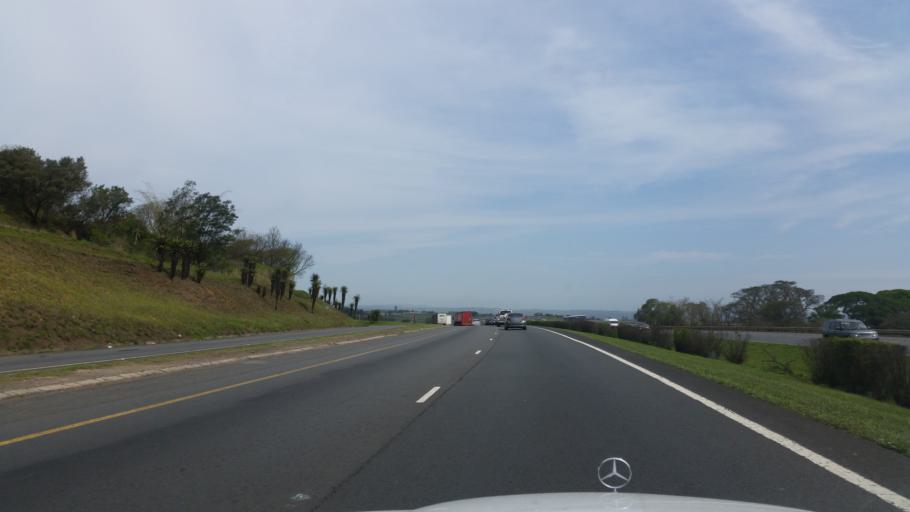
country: ZA
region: KwaZulu-Natal
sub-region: uMgungundlovu District Municipality
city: Camperdown
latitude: -29.7150
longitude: 30.4960
